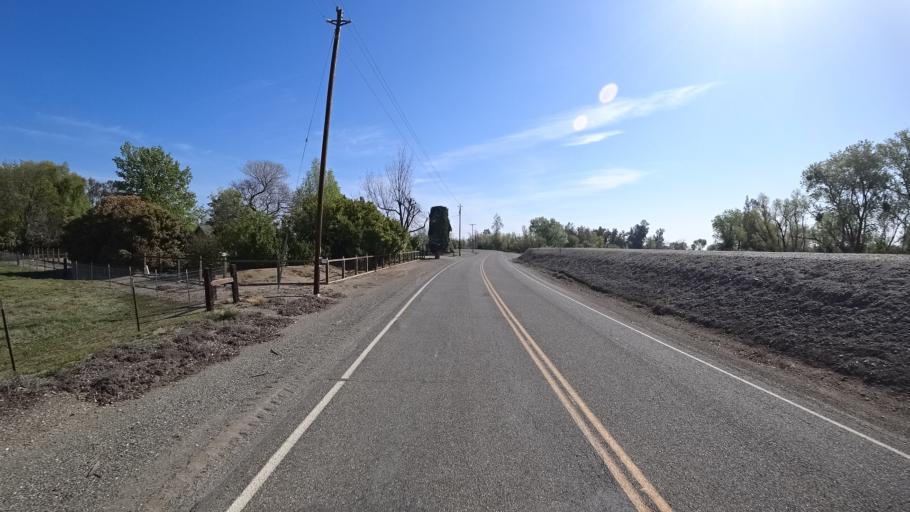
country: US
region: California
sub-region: Glenn County
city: Willows
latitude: 39.5426
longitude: -122.1671
